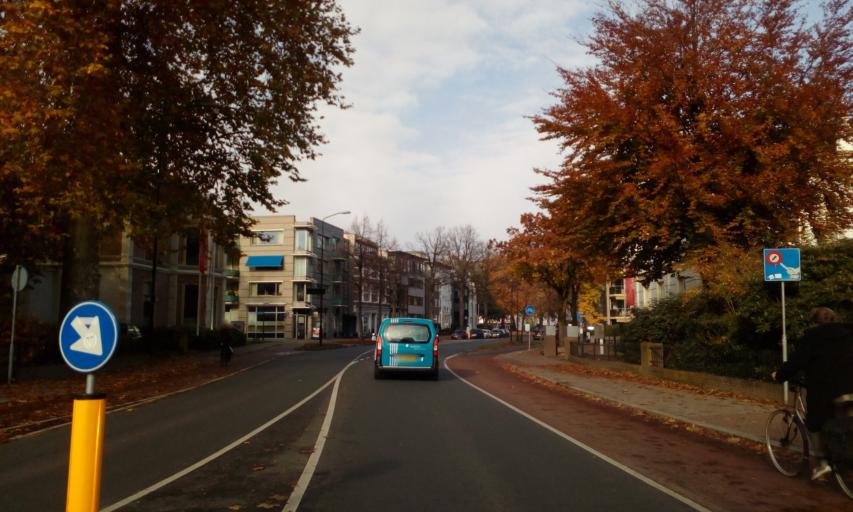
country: NL
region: Gelderland
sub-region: Gemeente Apeldoorn
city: Apeldoorn
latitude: 52.2179
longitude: 5.9559
